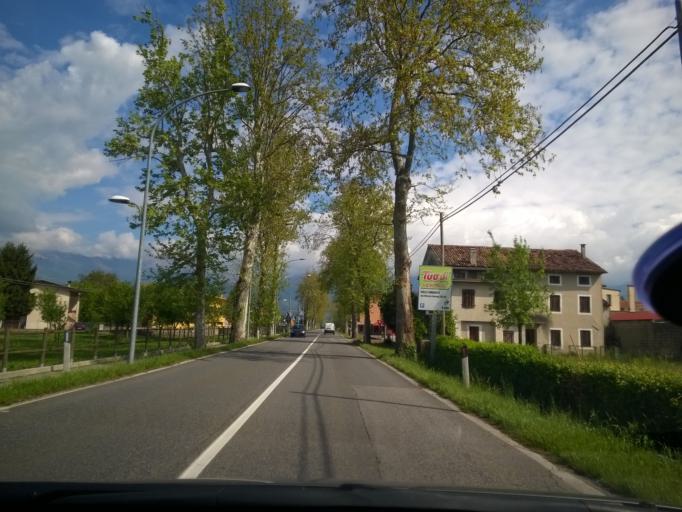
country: IT
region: Veneto
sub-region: Provincia di Treviso
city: Scomigo
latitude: 45.9384
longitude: 12.3224
